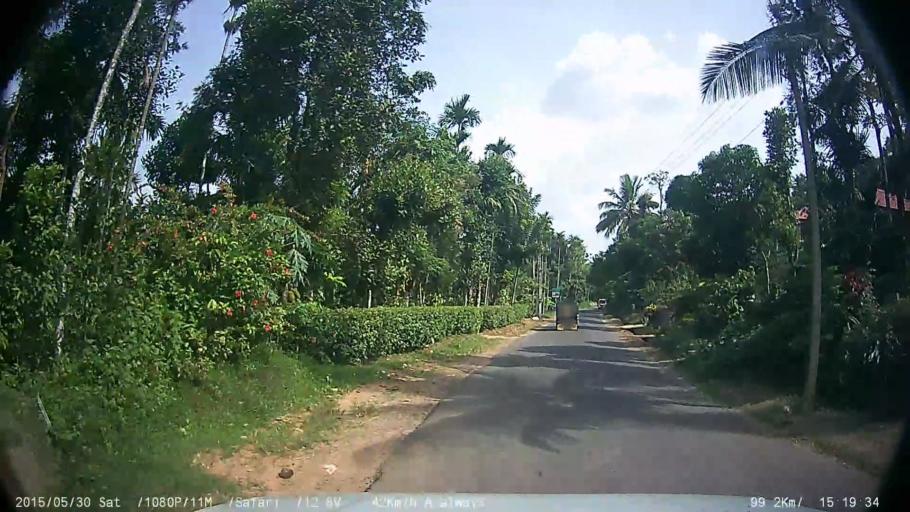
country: IN
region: Kerala
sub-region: Wayanad
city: Panamaram
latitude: 11.7579
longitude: 76.0643
